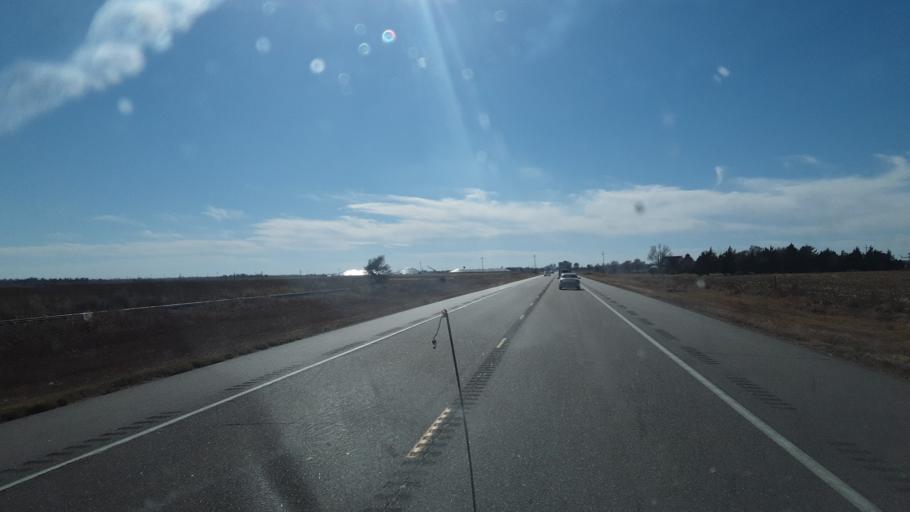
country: US
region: Kansas
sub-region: Pawnee County
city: Larned
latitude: 38.2119
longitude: -99.0553
